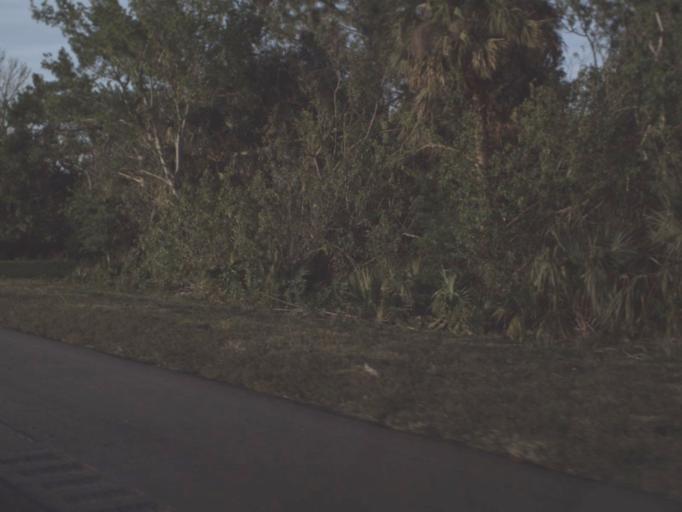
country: US
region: Florida
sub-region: Brevard County
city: Mims
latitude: 28.7481
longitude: -80.8872
